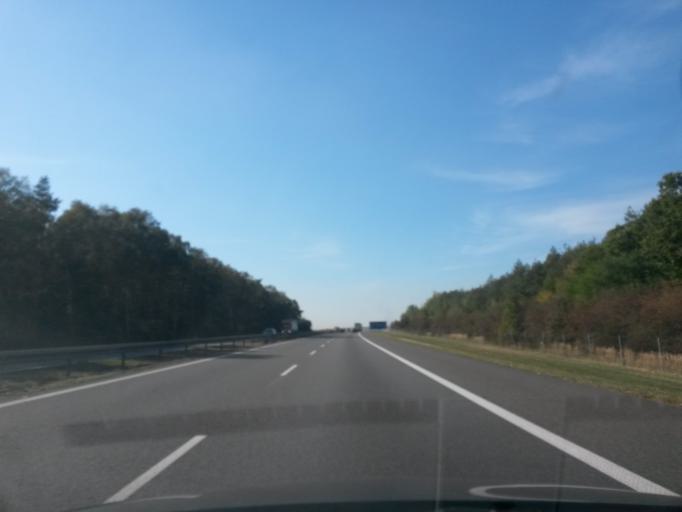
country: PL
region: Opole Voivodeship
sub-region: Powiat strzelecki
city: Strzelce Opolskie
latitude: 50.4533
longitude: 18.3010
